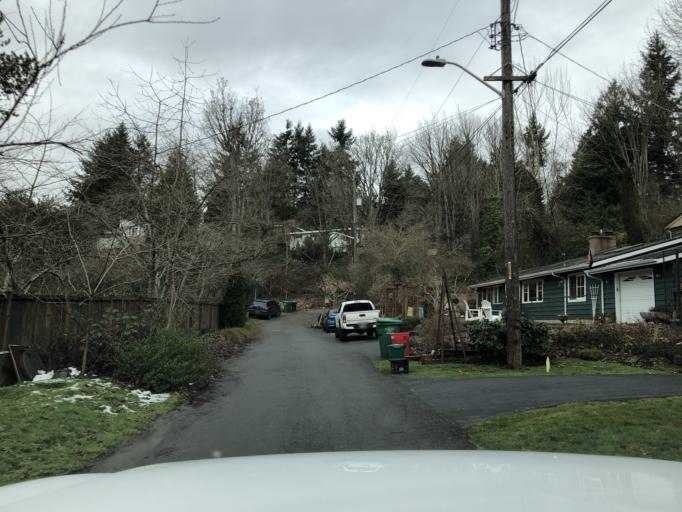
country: US
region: Washington
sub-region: King County
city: Inglewood-Finn Hill
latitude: 47.7041
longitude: -122.2800
